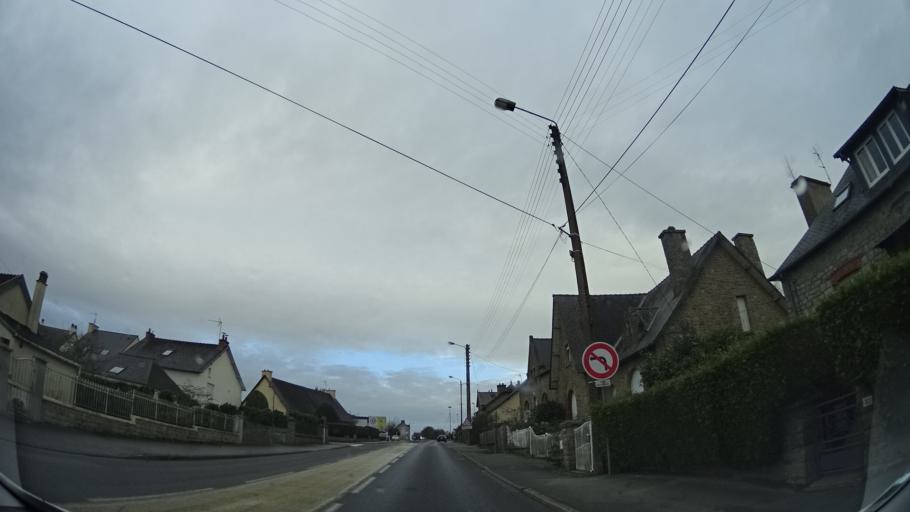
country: FR
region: Brittany
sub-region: Departement des Cotes-d'Armor
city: Quevert
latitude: 48.4476
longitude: -2.0722
